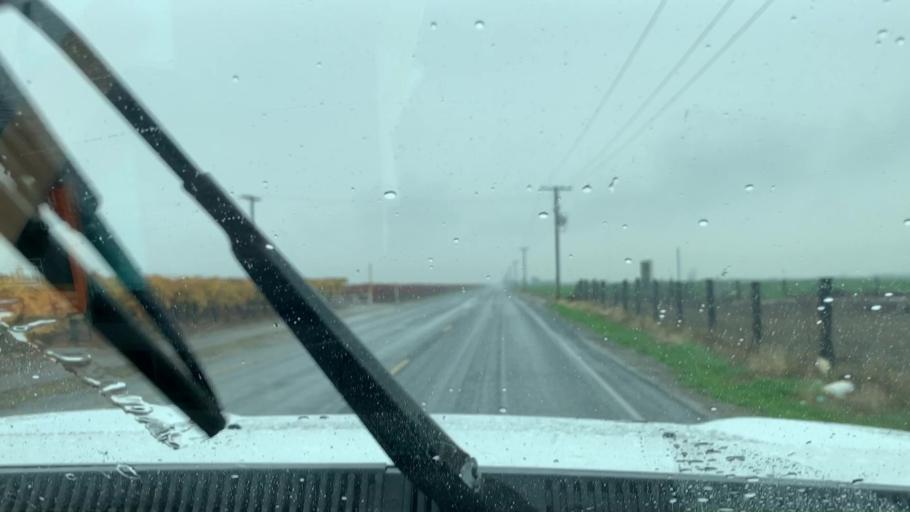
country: US
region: California
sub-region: Tulare County
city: Earlimart
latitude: 35.8919
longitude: -119.2942
